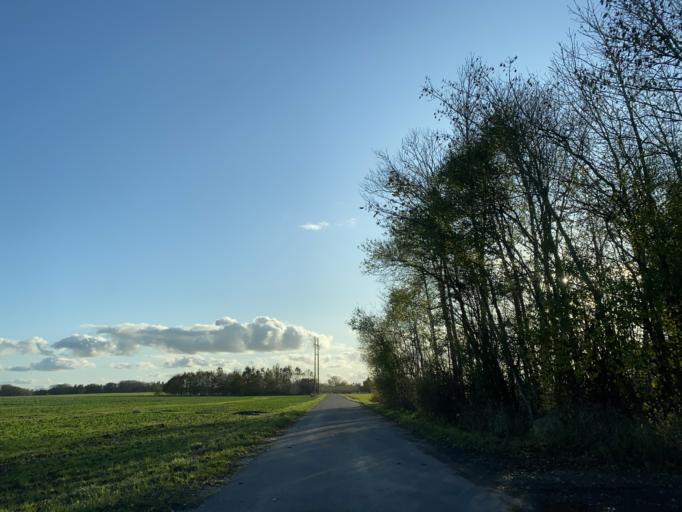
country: DK
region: Central Jutland
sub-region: Viborg Kommune
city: Bjerringbro
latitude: 56.3217
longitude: 9.7019
